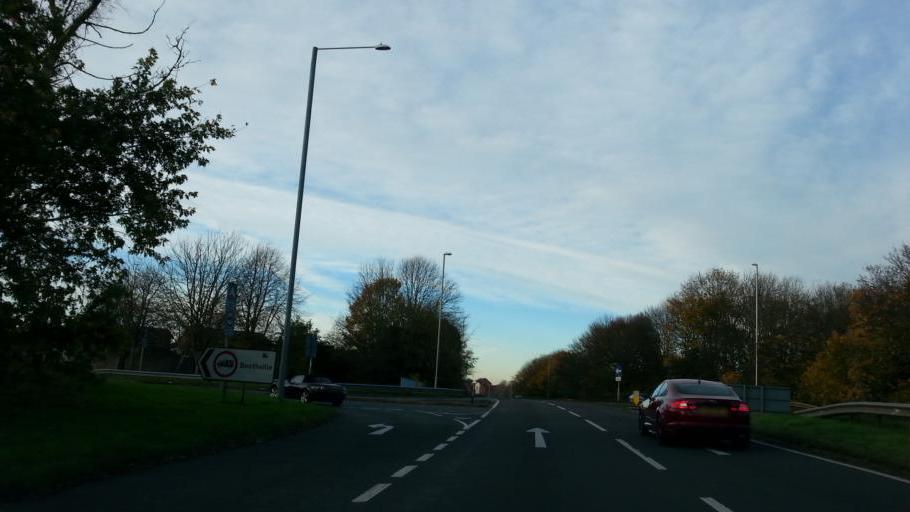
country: GB
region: England
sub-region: Northamptonshire
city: Northampton
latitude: 52.2700
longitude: -0.8444
